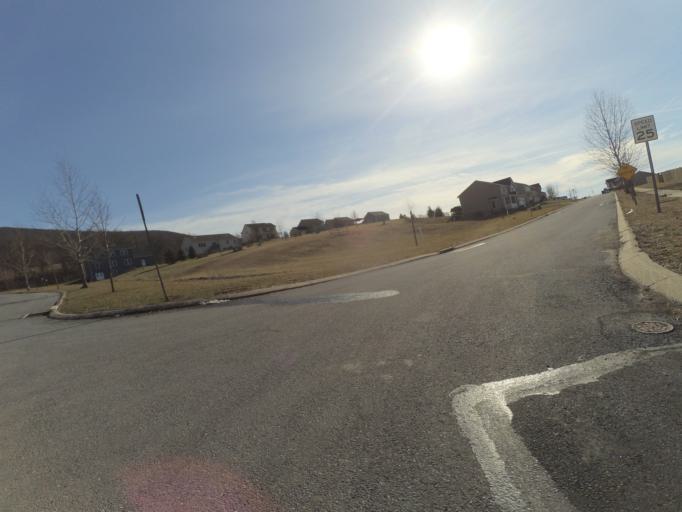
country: US
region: Pennsylvania
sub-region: Centre County
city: Lemont
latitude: 40.8208
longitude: -77.8085
